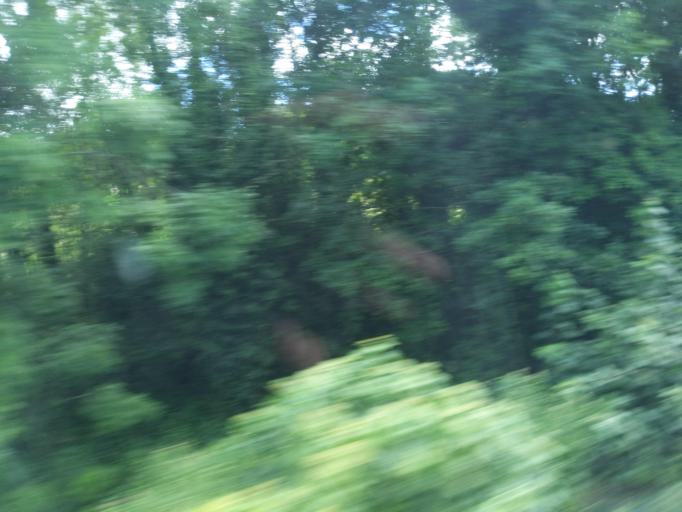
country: GB
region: England
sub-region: Cornwall
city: Lostwithiel
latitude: 50.3776
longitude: -4.6813
